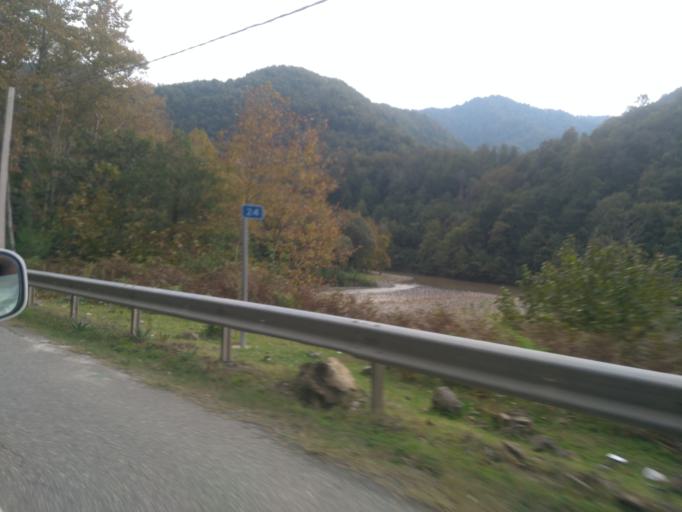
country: TR
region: Artvin
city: Camili
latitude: 41.5595
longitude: 41.8199
